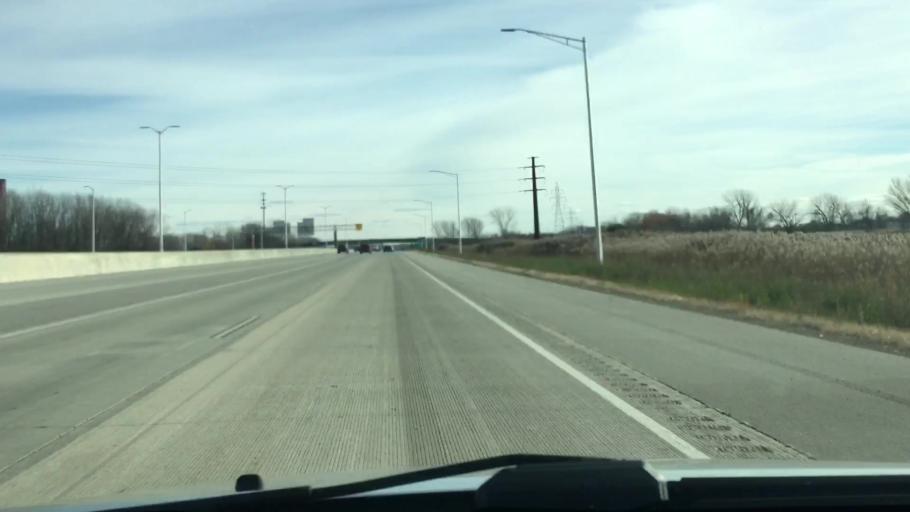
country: US
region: Wisconsin
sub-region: Brown County
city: Howard
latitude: 44.5557
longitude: -88.0472
